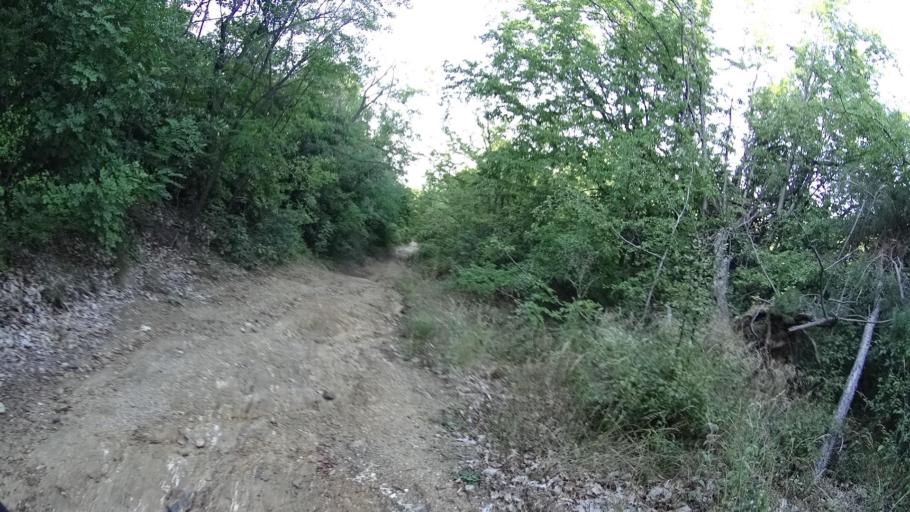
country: BG
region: Plovdiv
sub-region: Obshtina Plovdiv
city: Plovdiv
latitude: 42.0538
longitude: 24.6892
